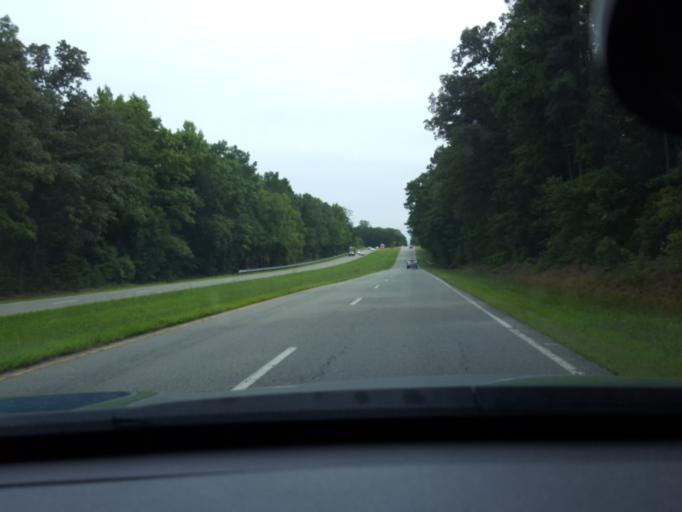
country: US
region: Virginia
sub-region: Caroline County
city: Bowling Green
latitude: 38.0052
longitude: -77.3342
